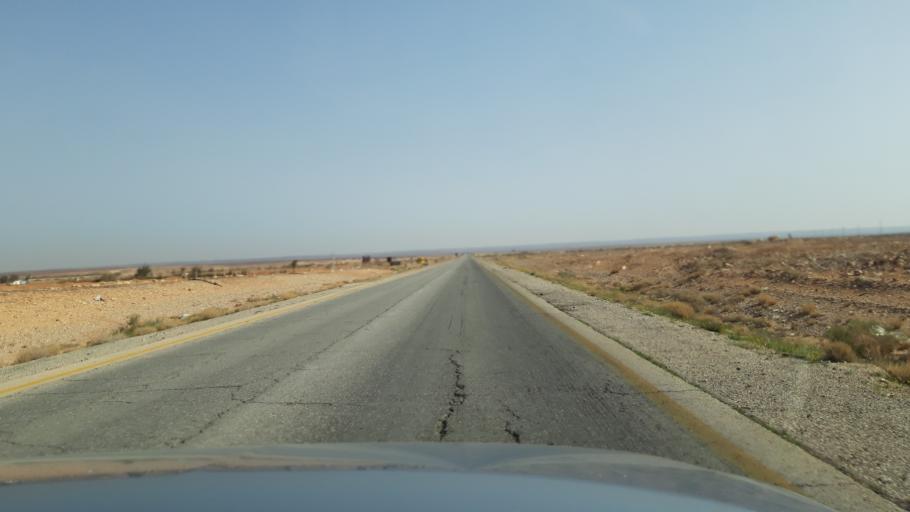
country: JO
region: Amman
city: Al Azraq ash Shamali
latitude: 31.7920
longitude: 36.5834
